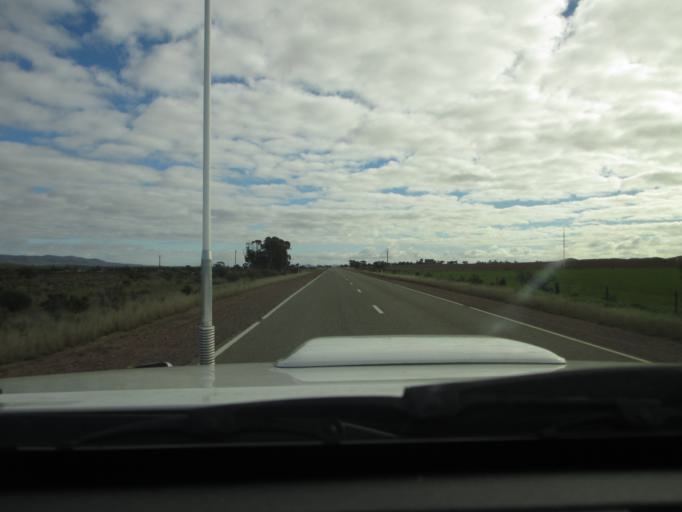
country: AU
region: South Australia
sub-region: Flinders Ranges
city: Quorn
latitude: -32.4342
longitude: 138.5334
